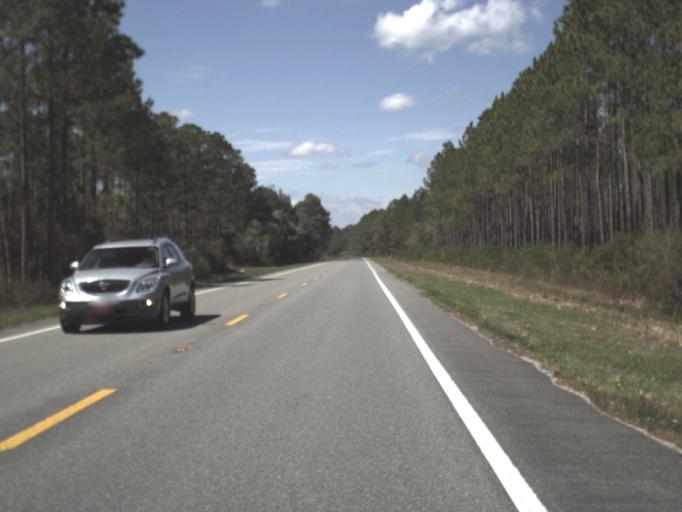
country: US
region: Florida
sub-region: Wakulla County
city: Crawfordville
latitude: 30.3239
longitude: -84.4565
